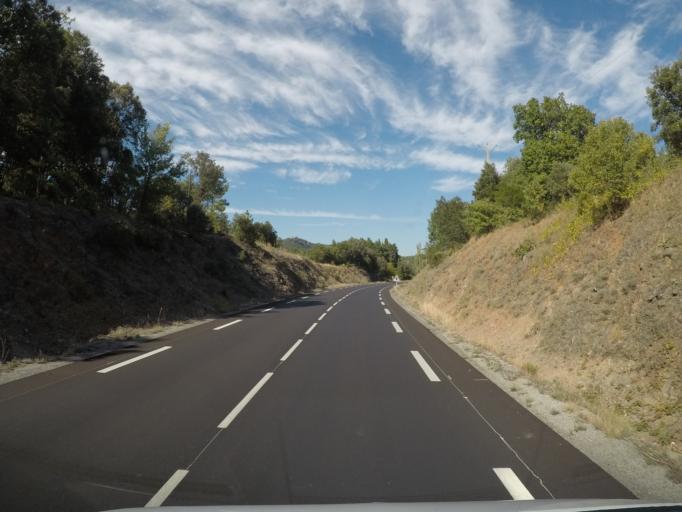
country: FR
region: Languedoc-Roussillon
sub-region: Departement du Gard
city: Sauve
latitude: 43.9744
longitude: 3.9247
